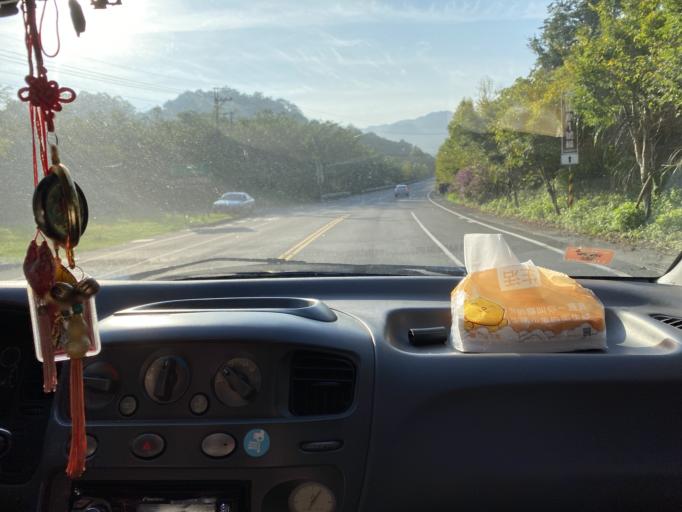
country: TW
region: Taiwan
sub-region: Keelung
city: Keelung
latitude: 25.0511
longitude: 121.7742
